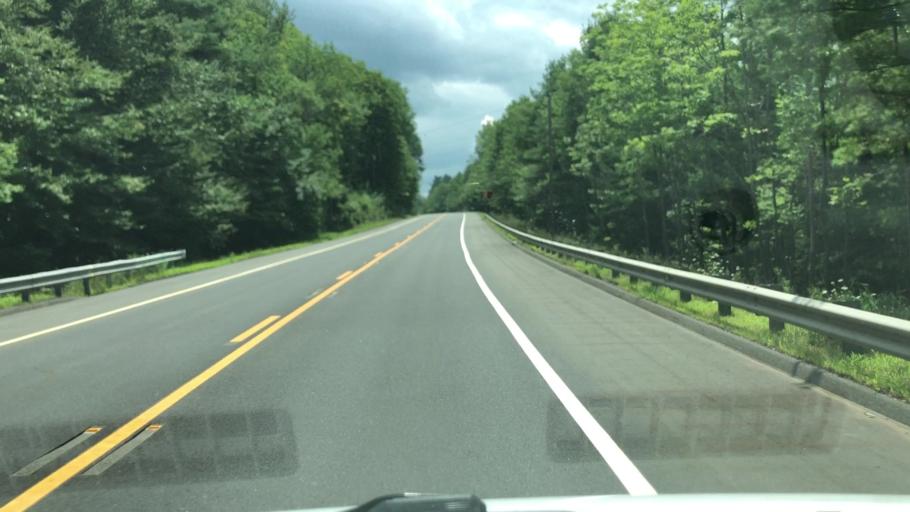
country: US
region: Massachusetts
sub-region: Franklin County
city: Ashfield
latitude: 42.4786
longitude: -72.8102
